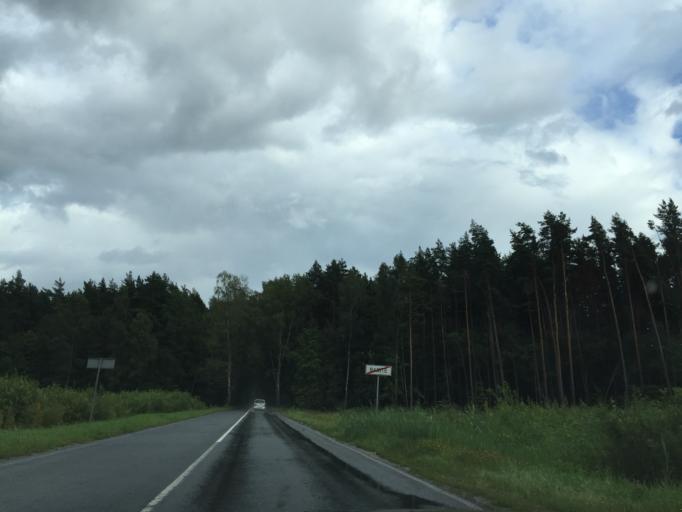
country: LV
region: Babite
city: Pinki
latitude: 56.9576
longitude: 23.9590
